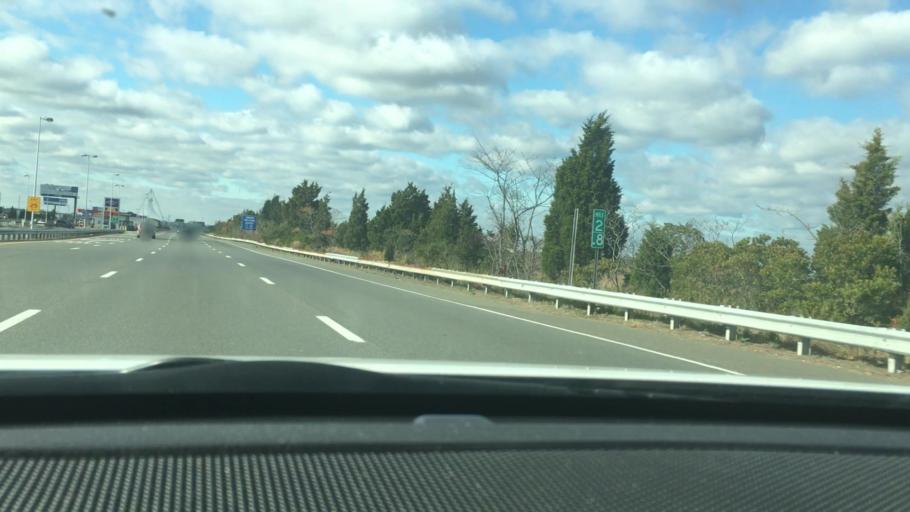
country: US
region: New Jersey
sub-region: Atlantic County
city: Pleasantville
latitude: 39.3794
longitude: -74.4869
